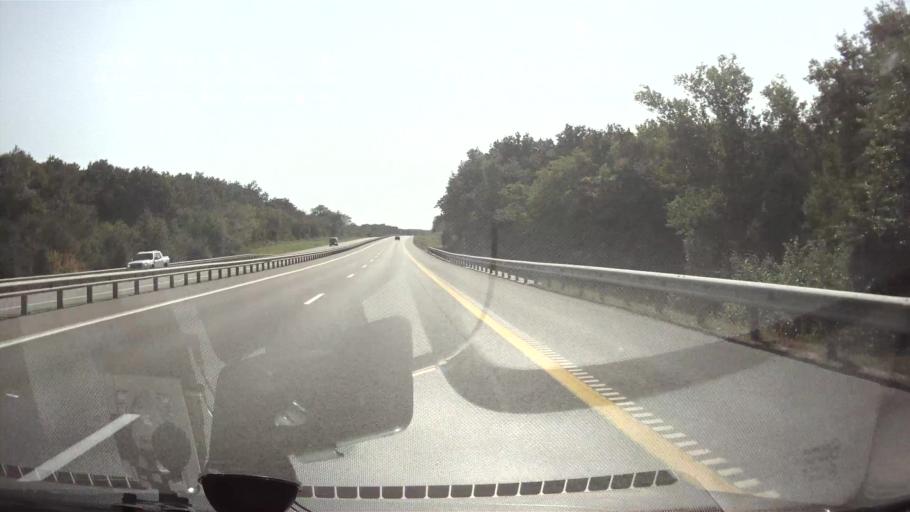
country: RU
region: Krasnodarskiy
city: Saratovskaya
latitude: 44.7451
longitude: 39.2252
